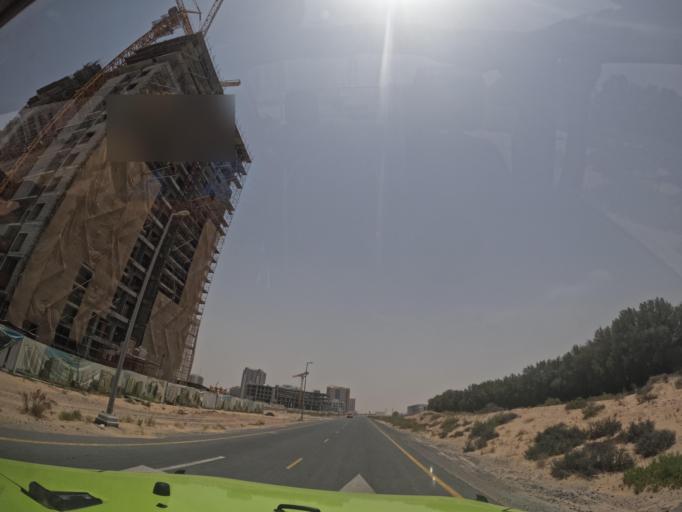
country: AE
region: Dubai
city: Dubai
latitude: 25.0926
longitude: 55.3740
